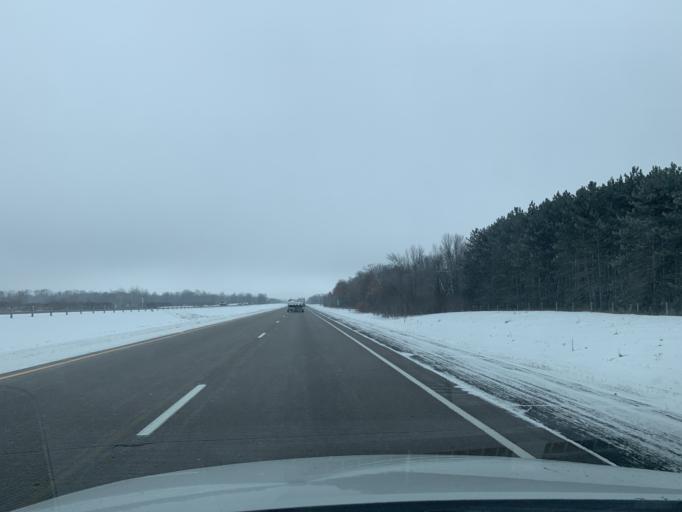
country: US
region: Minnesota
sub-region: Chisago County
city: Harris
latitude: 45.6257
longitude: -92.9921
